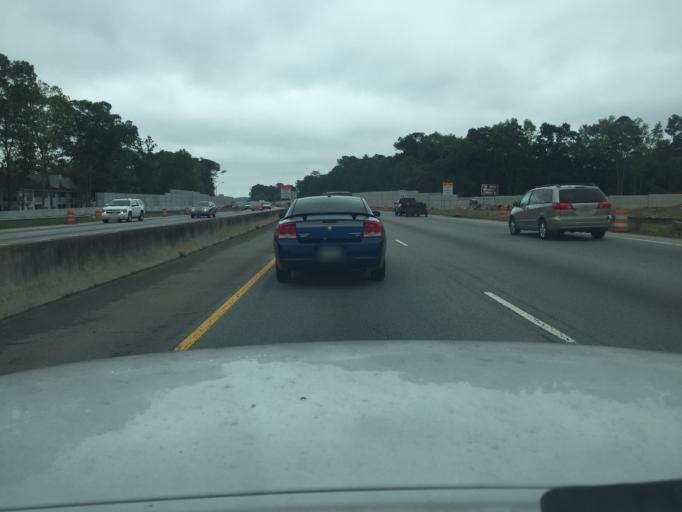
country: US
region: Georgia
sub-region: Chatham County
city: Georgetown
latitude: 31.9854
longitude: -81.2158
